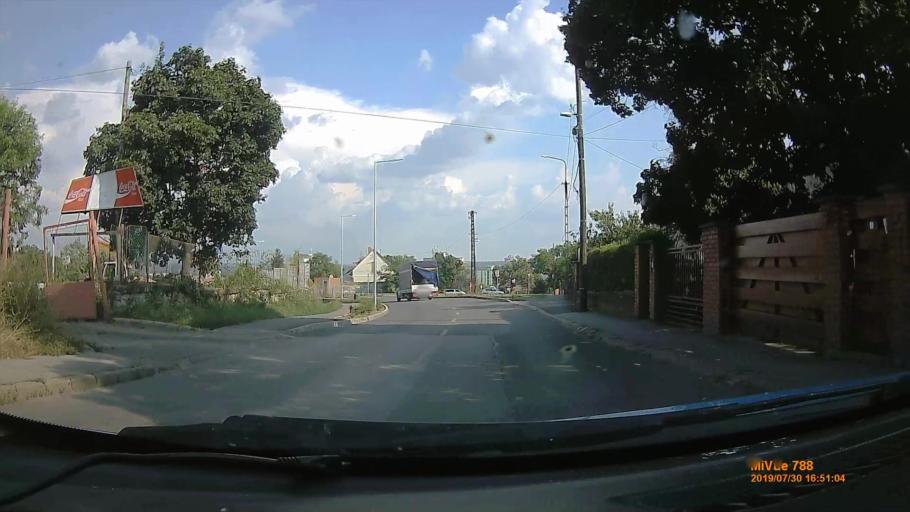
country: HU
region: Baranya
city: Pecs
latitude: 46.0798
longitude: 18.2107
